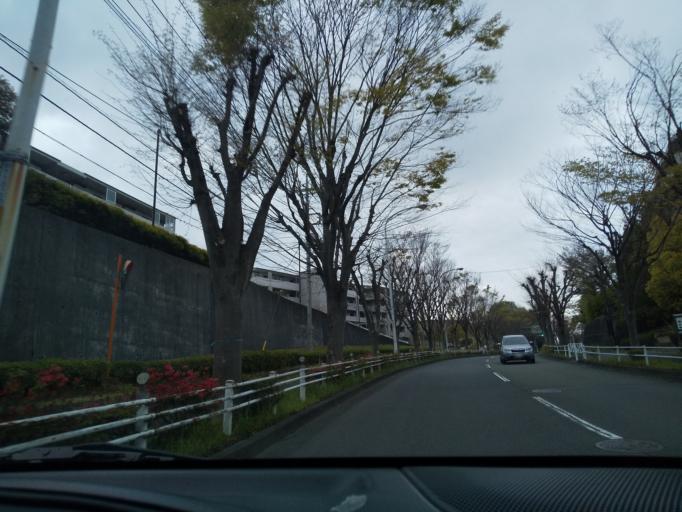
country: JP
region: Tokyo
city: Hino
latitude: 35.6043
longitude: 139.3824
